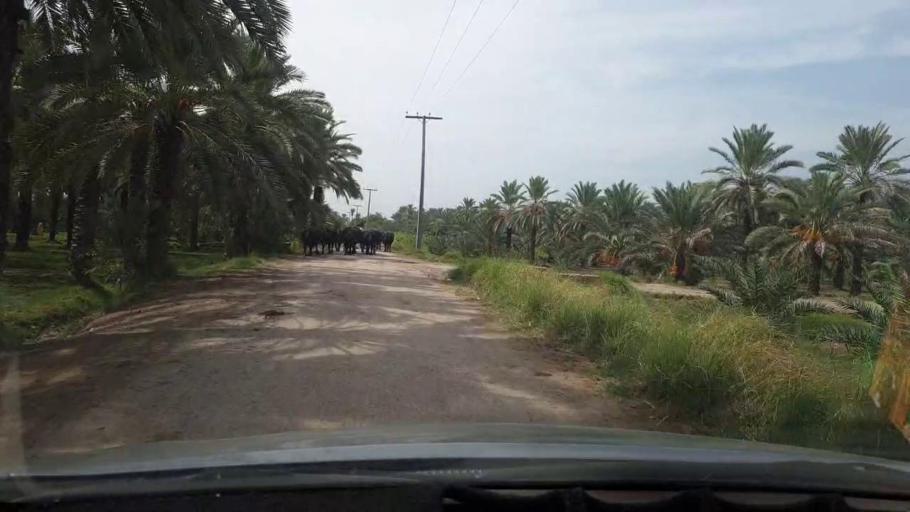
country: PK
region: Sindh
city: Khairpur
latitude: 27.4965
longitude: 68.7545
